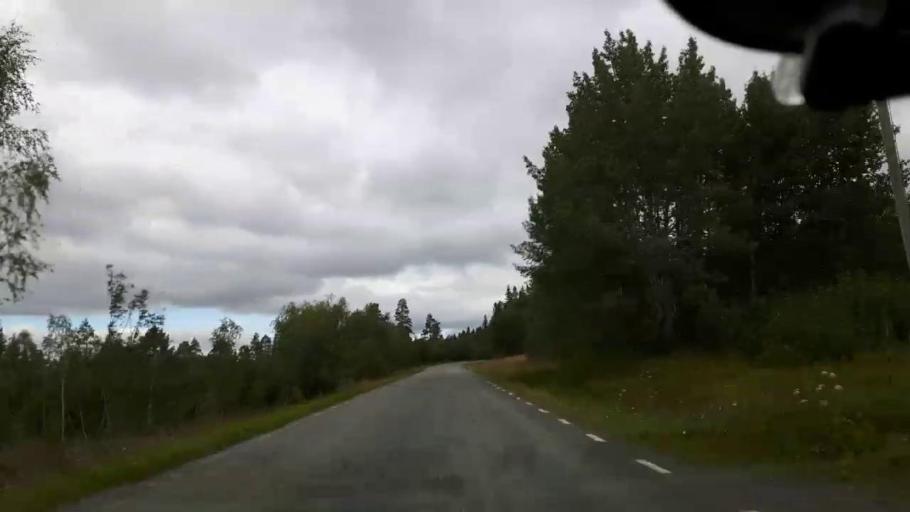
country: SE
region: Jaemtland
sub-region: Krokoms Kommun
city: Valla
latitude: 63.5197
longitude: 13.8739
